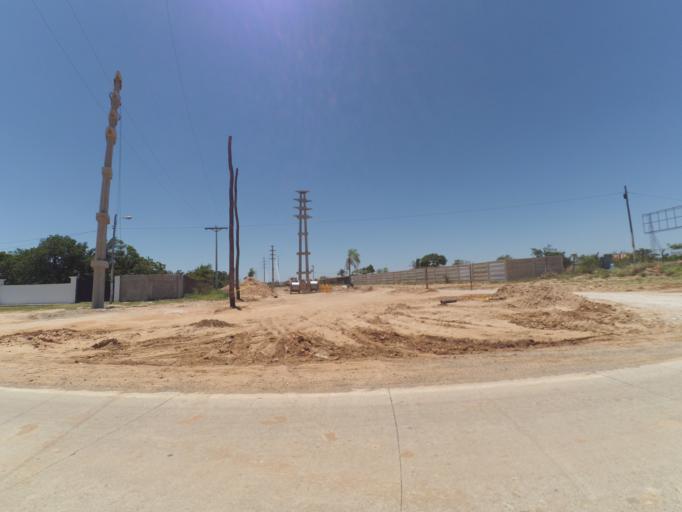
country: BO
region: Santa Cruz
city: Santa Cruz de la Sierra
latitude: -17.7659
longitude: -63.2388
